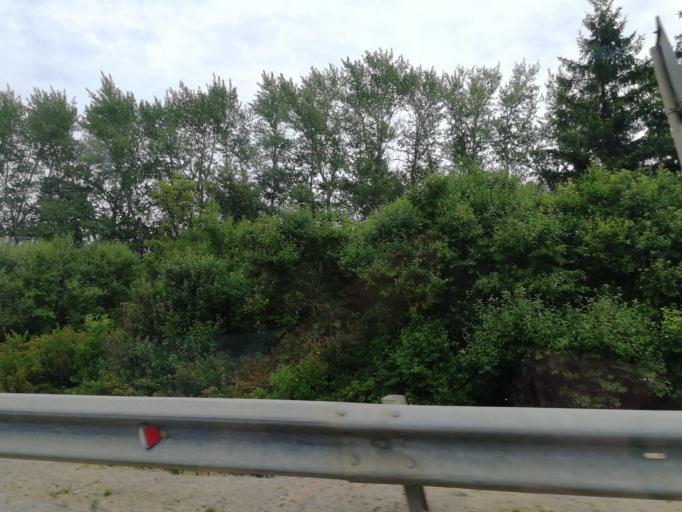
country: RU
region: Tula
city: Bogoroditsk
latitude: 53.7208
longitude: 38.1054
